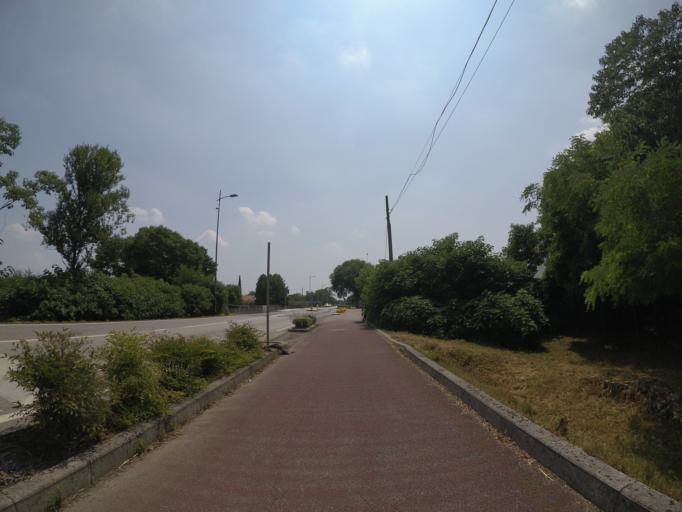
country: IT
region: Friuli Venezia Giulia
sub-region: Provincia di Udine
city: Basiliano-Vissandone
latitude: 46.0239
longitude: 13.1052
